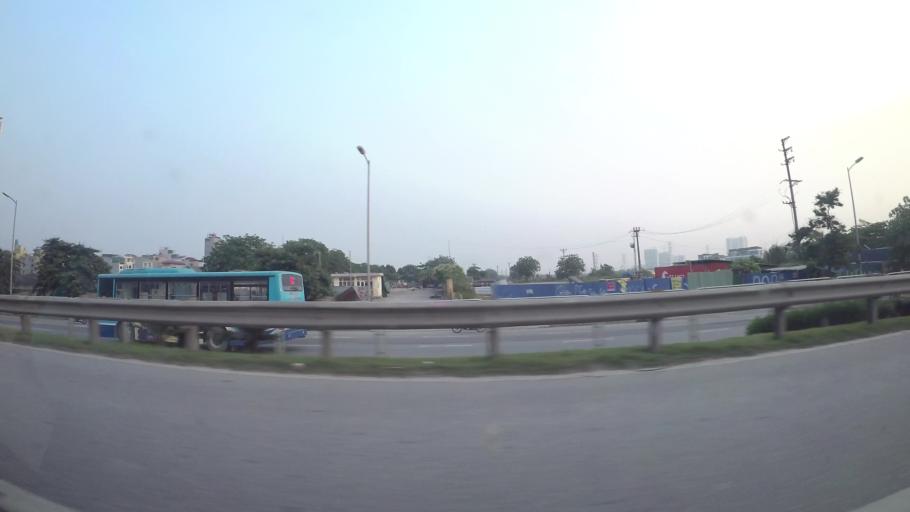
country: VN
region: Ha Noi
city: Van Dien
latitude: 20.9639
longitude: 105.8620
